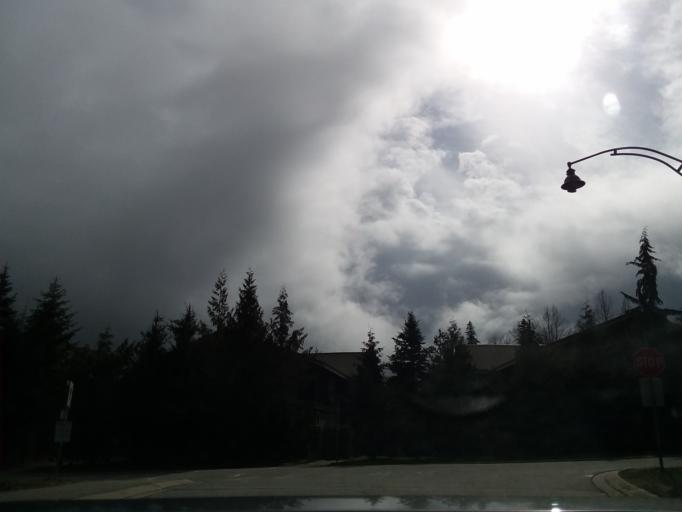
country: CA
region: British Columbia
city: Whistler
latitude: 50.1319
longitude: -122.9503
